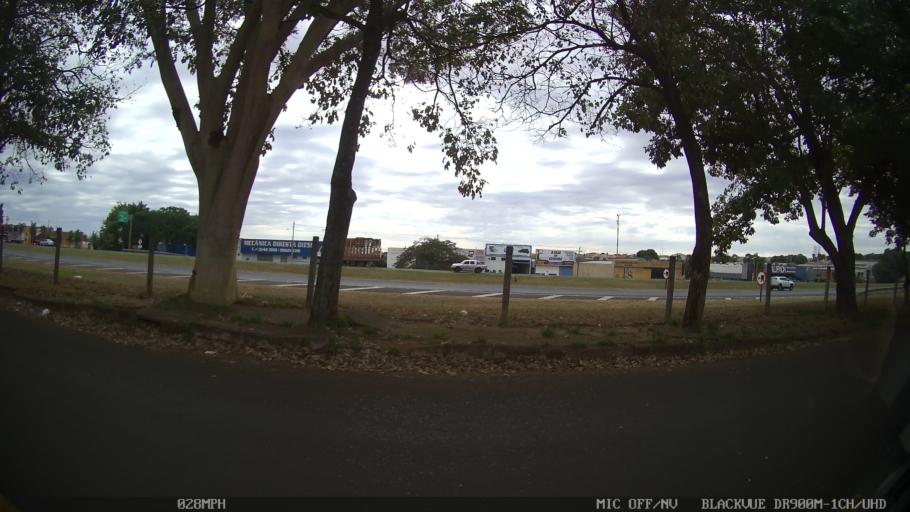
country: BR
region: Sao Paulo
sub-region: Sao Jose Do Rio Preto
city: Sao Jose do Rio Preto
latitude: -20.8095
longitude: -49.5008
